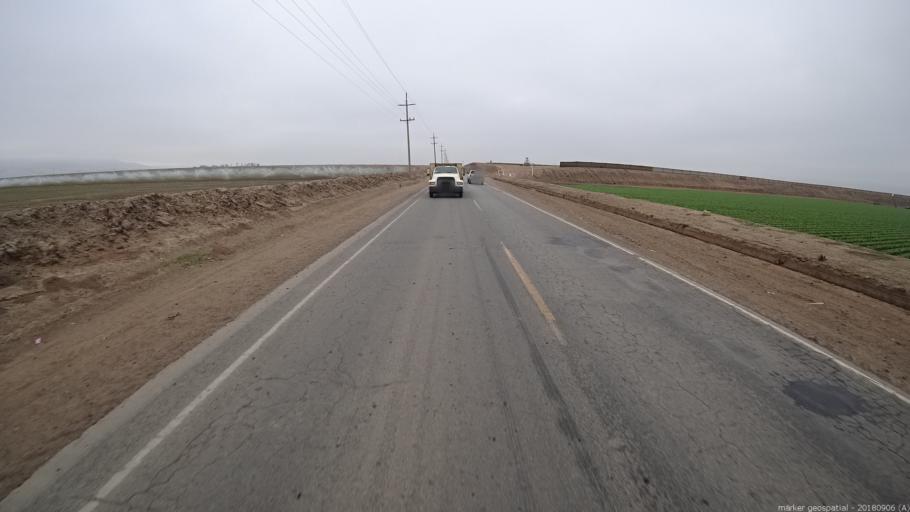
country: US
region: California
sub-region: Monterey County
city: Salinas
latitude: 36.6606
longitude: -121.5903
